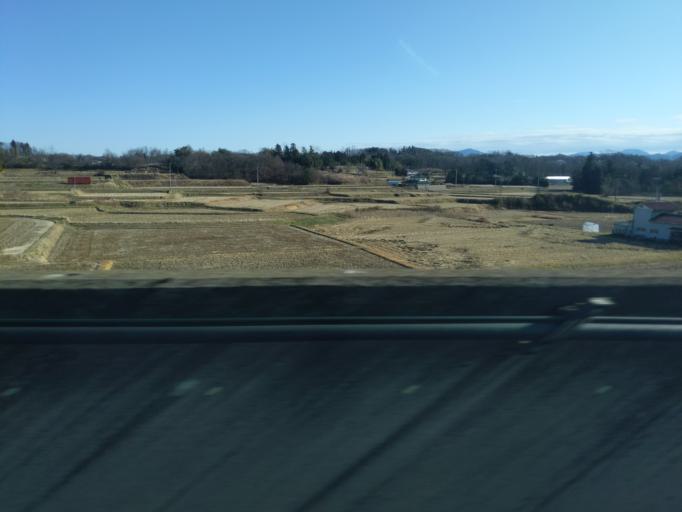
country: JP
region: Fukushima
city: Koriyama
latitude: 37.4441
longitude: 140.4036
